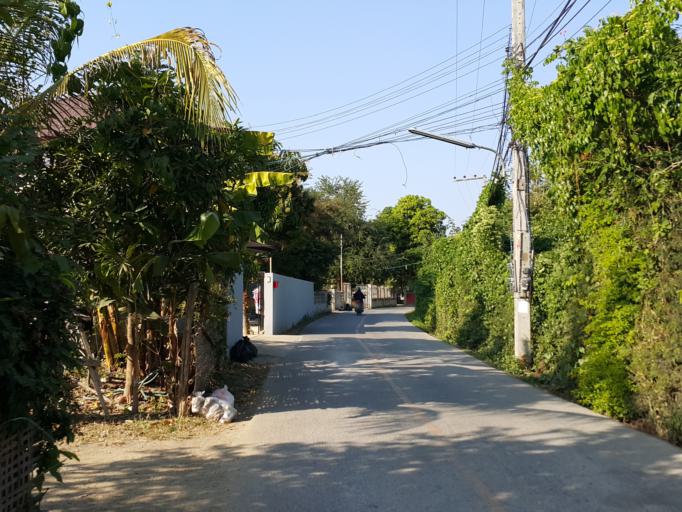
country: TH
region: Chiang Mai
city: San Kamphaeng
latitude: 18.7861
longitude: 99.0934
